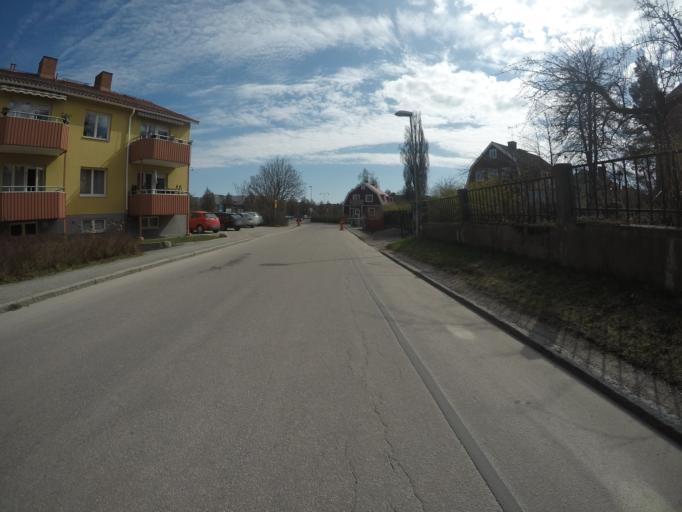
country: SE
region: Vaestmanland
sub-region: Vasteras
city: Vasteras
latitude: 59.6178
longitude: 16.5389
